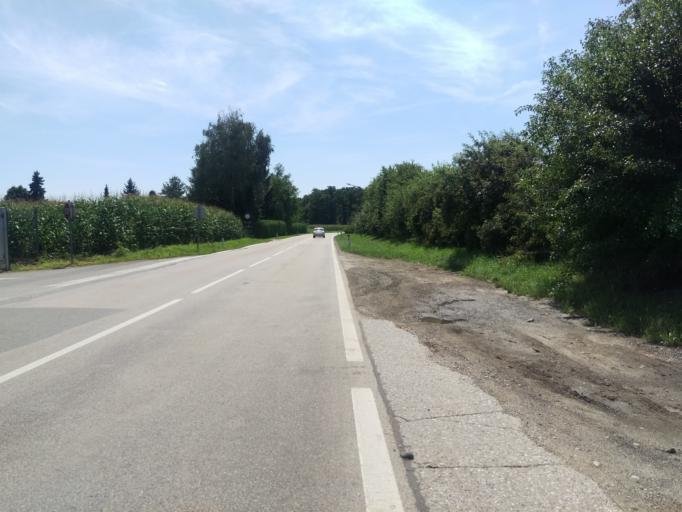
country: AT
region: Styria
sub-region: Politischer Bezirk Graz-Umgebung
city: Zettling
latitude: 46.9743
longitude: 15.4388
